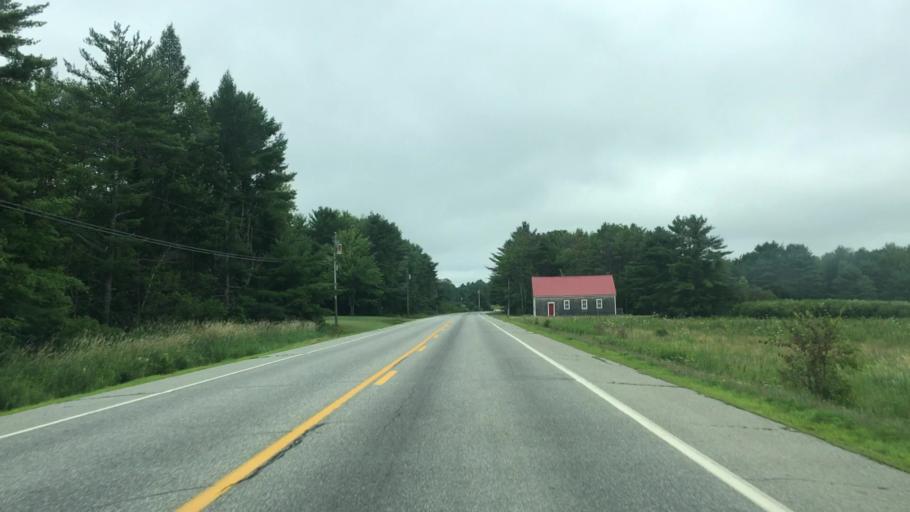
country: US
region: Maine
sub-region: Sagadahoc County
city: Richmond
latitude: 44.1153
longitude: -69.7332
